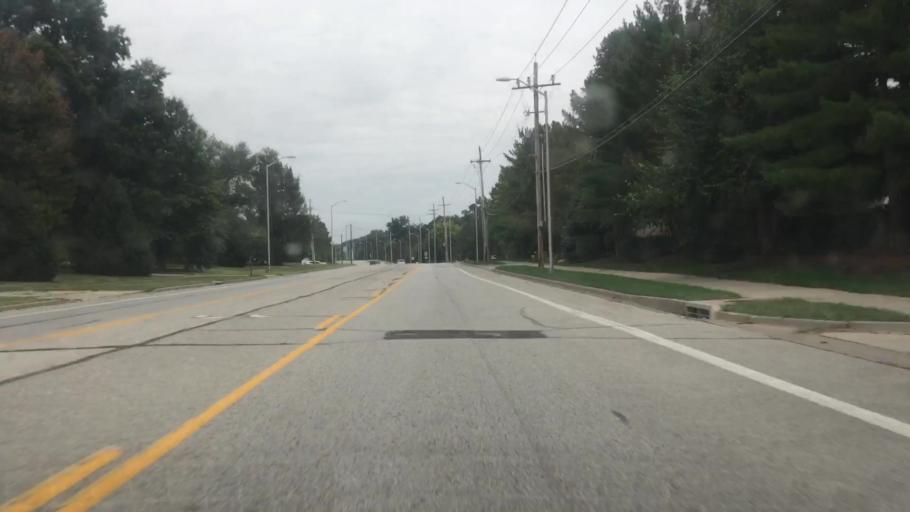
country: US
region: Kansas
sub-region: Johnson County
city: Lenexa
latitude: 38.9986
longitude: -94.7729
